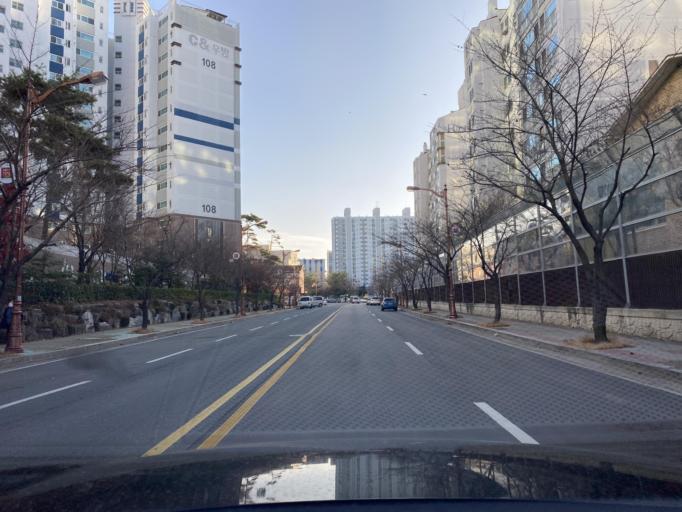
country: KR
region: Chungcheongnam-do
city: Yesan
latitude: 36.6962
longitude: 126.8333
